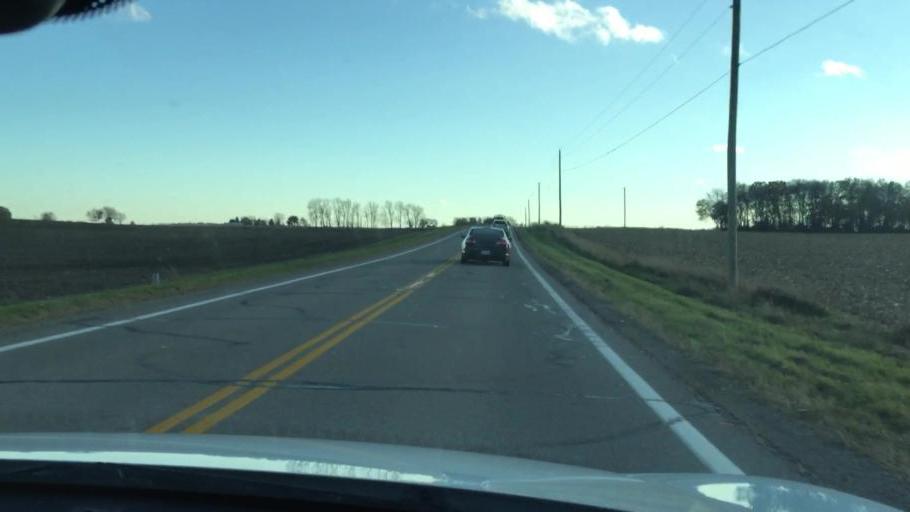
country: US
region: Ohio
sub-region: Champaign County
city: North Lewisburg
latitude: 40.1592
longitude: -83.5273
